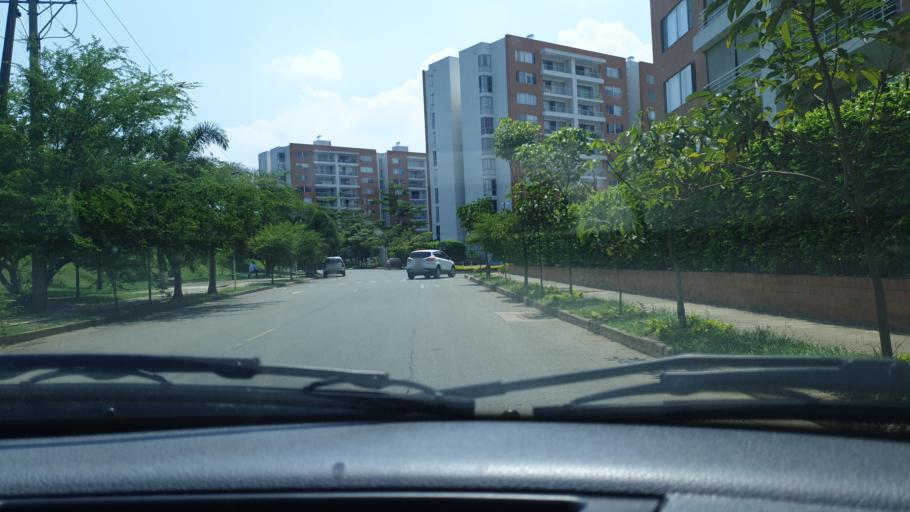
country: CO
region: Valle del Cauca
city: Cali
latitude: 3.3642
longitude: -76.5223
